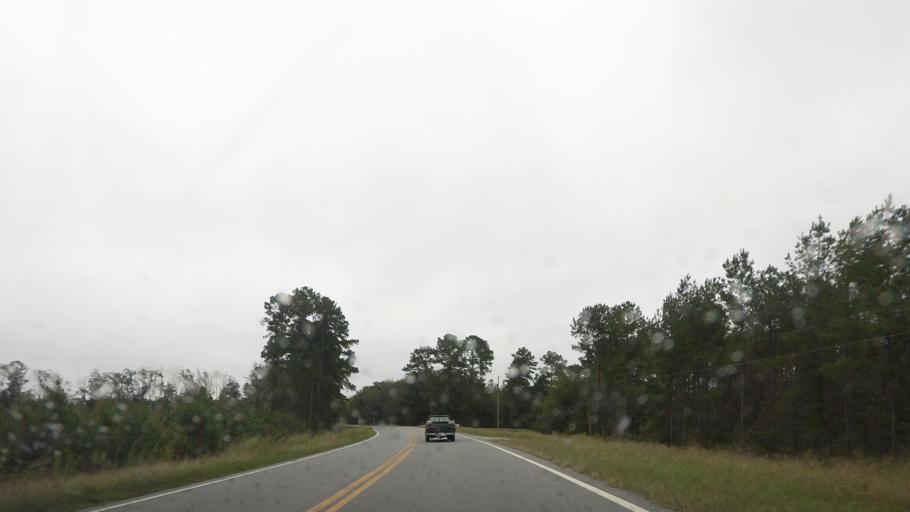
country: US
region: Georgia
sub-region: Berrien County
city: Enigma
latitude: 31.4336
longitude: -83.2423
